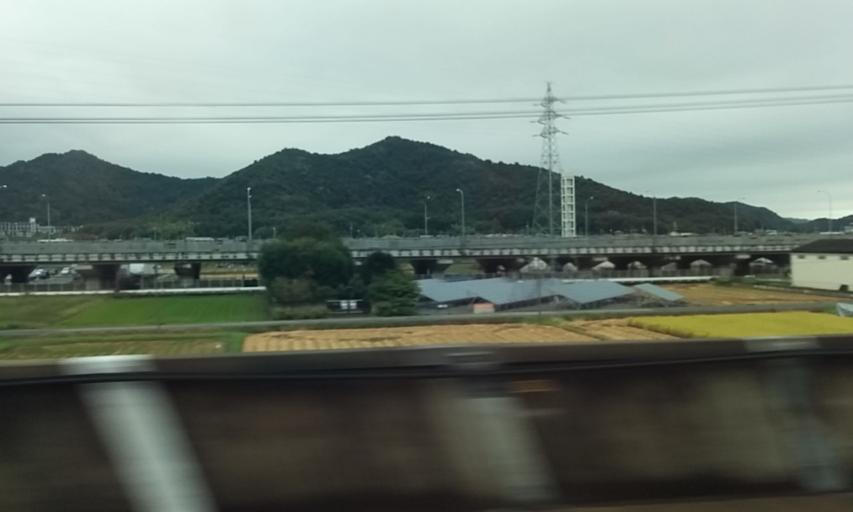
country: JP
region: Hyogo
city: Shirahamacho-usazakiminami
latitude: 34.7936
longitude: 134.7626
